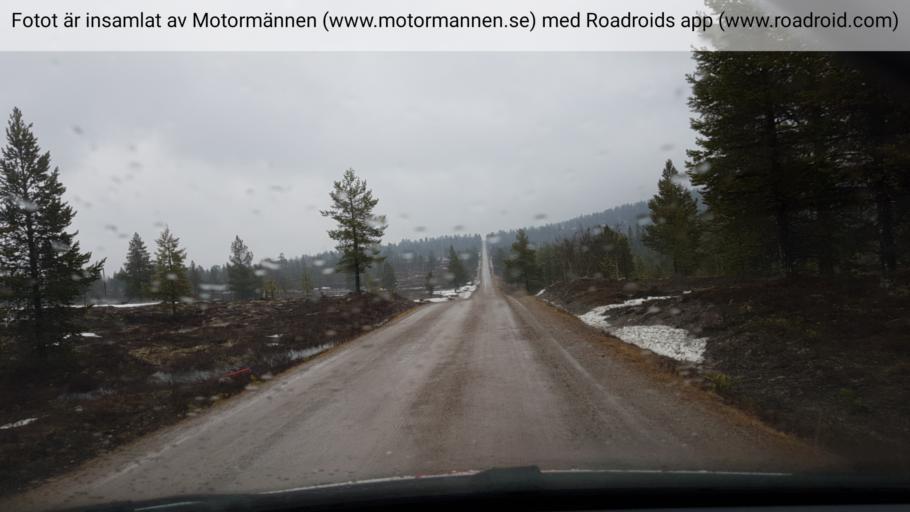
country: NO
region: Hedmark
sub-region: Engerdal
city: Engerdal
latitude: 62.1326
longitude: 12.9189
